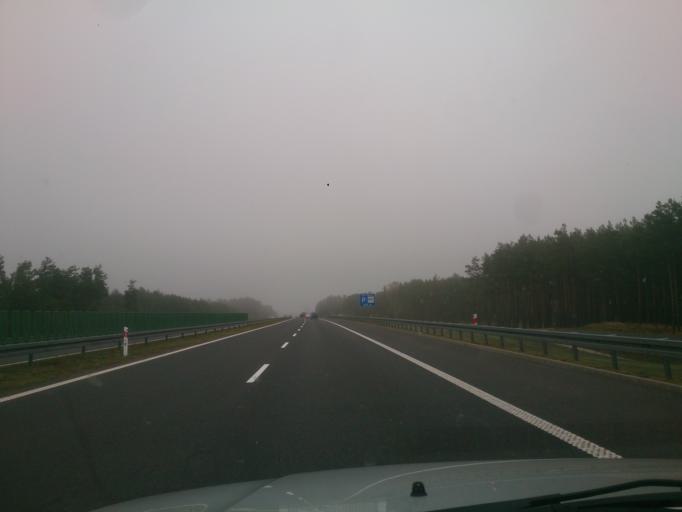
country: PL
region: Kujawsko-Pomorskie
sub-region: Powiat swiecki
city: Warlubie
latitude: 53.6203
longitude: 18.6357
